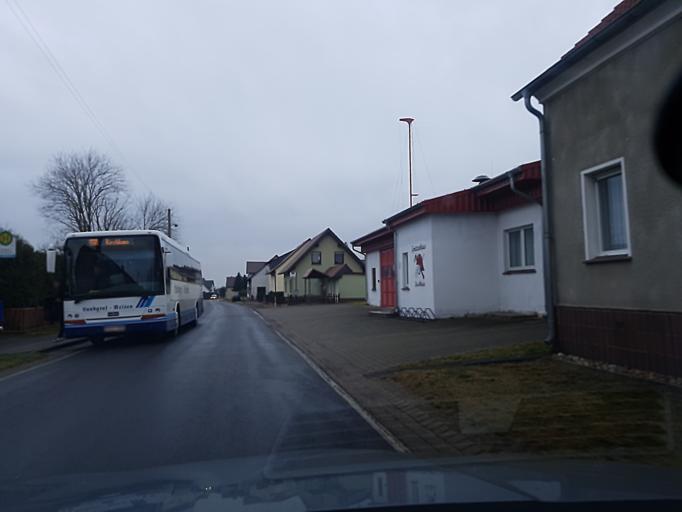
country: DE
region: Brandenburg
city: Schilda
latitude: 51.6465
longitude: 13.3881
